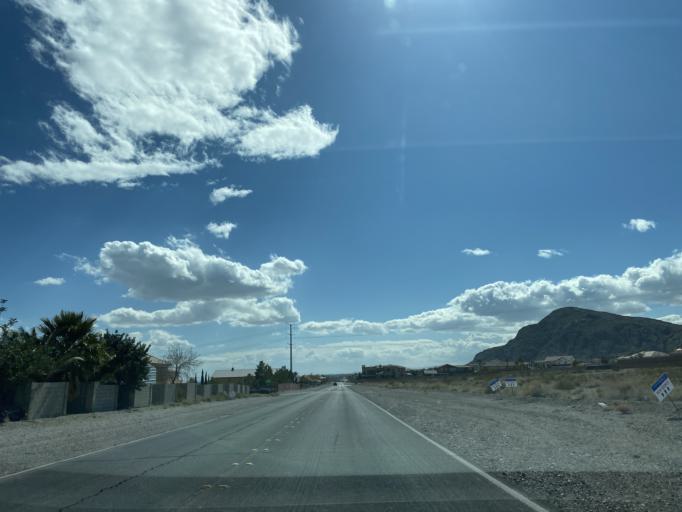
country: US
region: Nevada
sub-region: Clark County
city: Summerlin South
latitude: 36.2547
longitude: -115.3062
